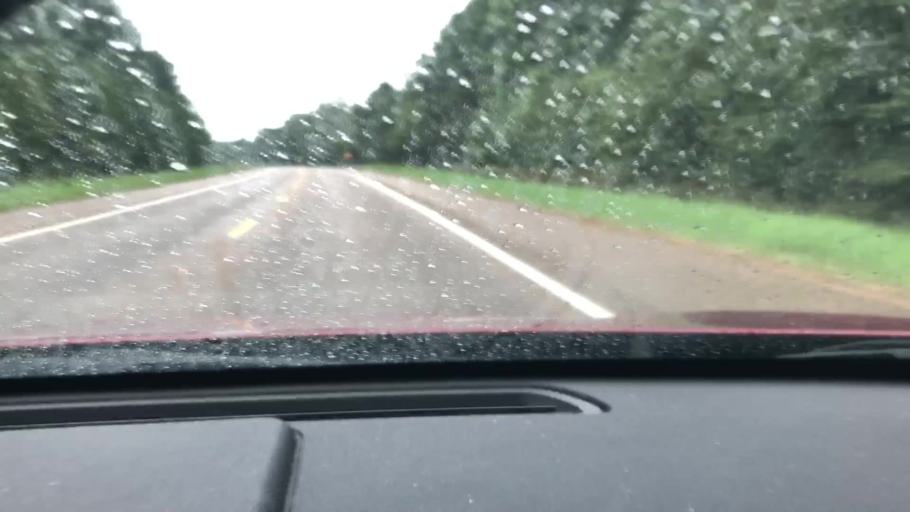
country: US
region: Arkansas
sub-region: Columbia County
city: Magnolia
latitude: 33.2978
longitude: -93.2615
